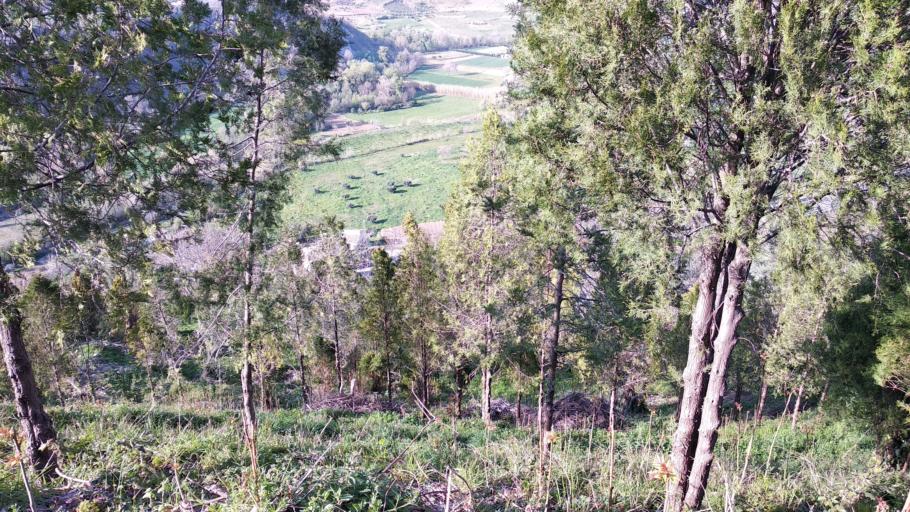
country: IT
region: Calabria
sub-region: Provincia di Cosenza
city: San Marco Argentano
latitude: 39.5591
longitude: 16.1170
